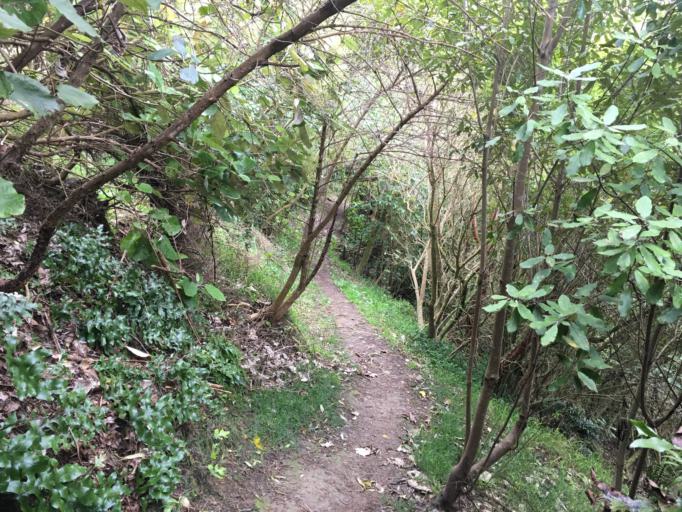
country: NZ
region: Wellington
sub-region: Wellington City
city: Kelburn
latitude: -41.2736
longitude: 174.7702
